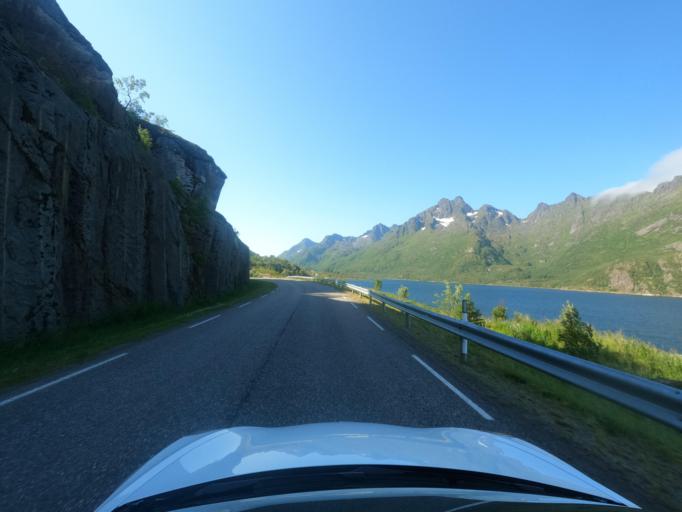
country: NO
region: Nordland
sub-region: Hadsel
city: Stokmarknes
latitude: 68.4396
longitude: 15.1870
